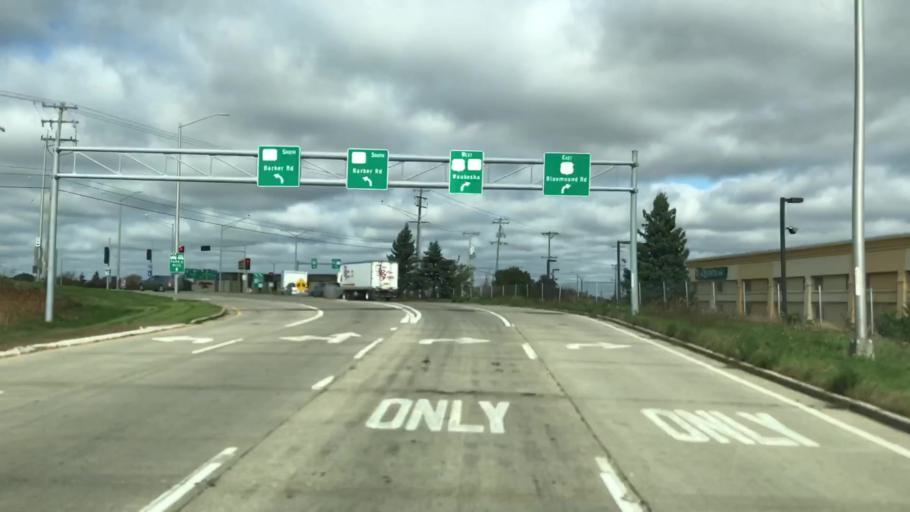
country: US
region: Wisconsin
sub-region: Waukesha County
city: Brookfield
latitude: 43.0341
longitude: -88.1660
